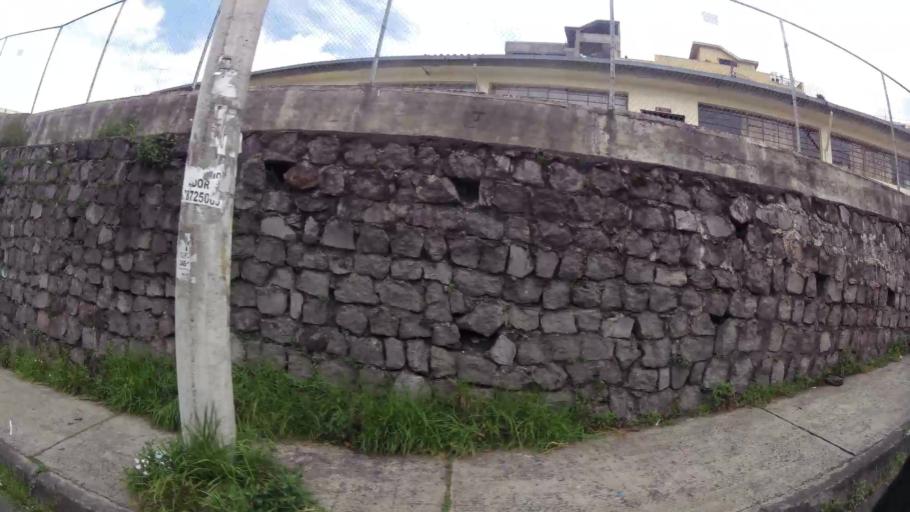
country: EC
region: Pichincha
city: Quito
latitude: -0.2137
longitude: -78.5189
